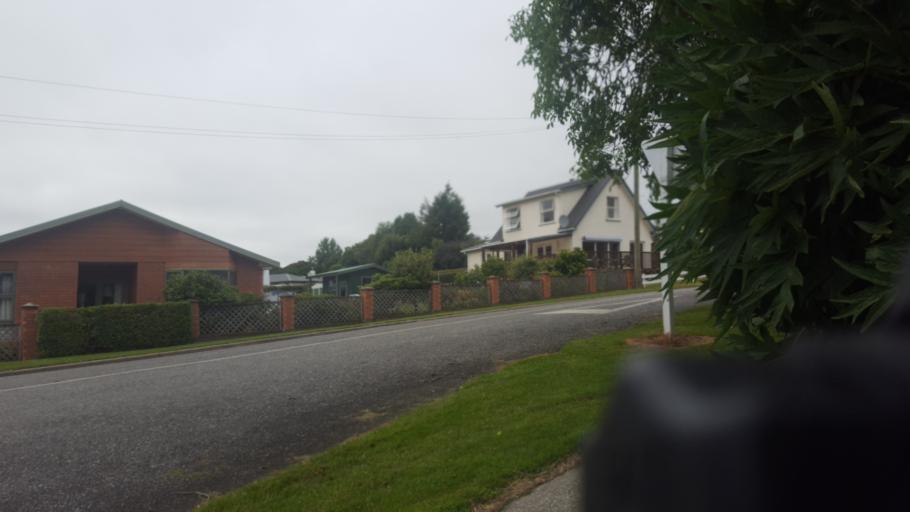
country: NZ
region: Otago
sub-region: Queenstown-Lakes District
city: Kingston
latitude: -45.5392
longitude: 169.3152
